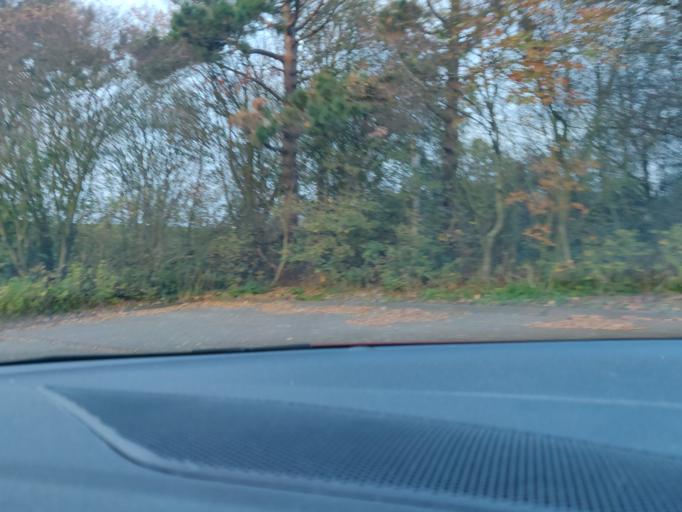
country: DE
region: Lower Saxony
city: Cuxhaven
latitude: 53.8886
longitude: 8.6622
